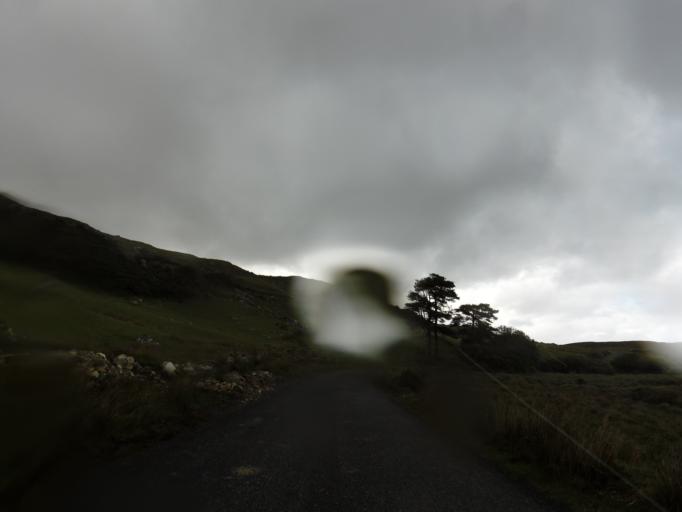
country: IE
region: Connaught
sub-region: County Galway
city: Oughterard
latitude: 53.3917
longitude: -9.3399
